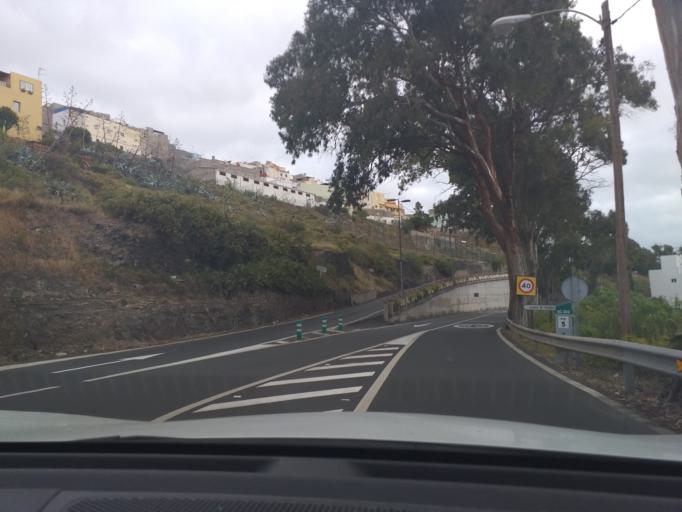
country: ES
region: Canary Islands
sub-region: Provincia de Las Palmas
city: Arucas
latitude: 28.1104
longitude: -15.4931
